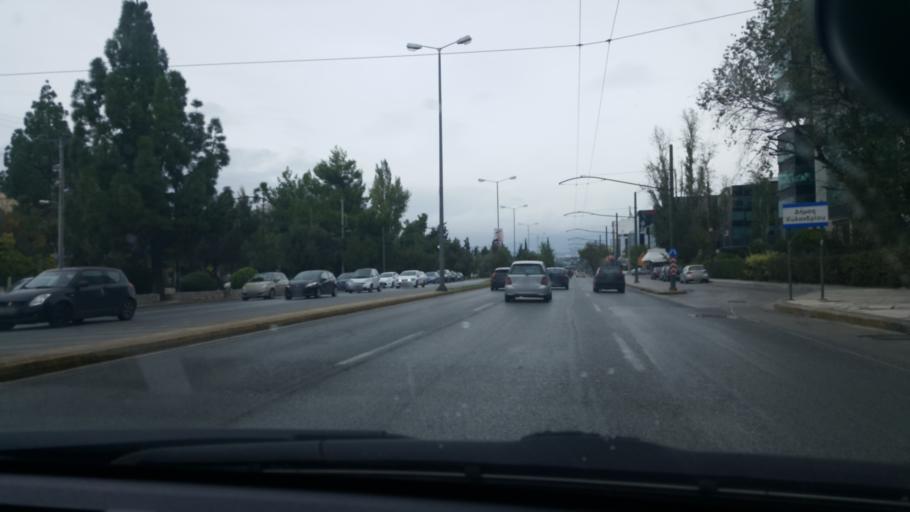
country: GR
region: Attica
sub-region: Nomarchia Athinas
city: Neo Psychiko
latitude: 38.0100
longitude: 23.7803
